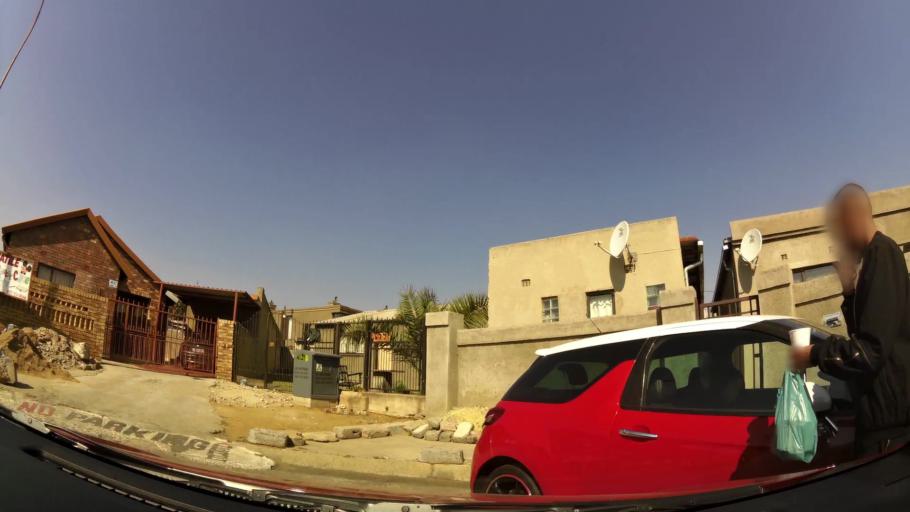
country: ZA
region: Gauteng
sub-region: City of Johannesburg Metropolitan Municipality
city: Johannesburg
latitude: -26.2438
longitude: 27.9549
